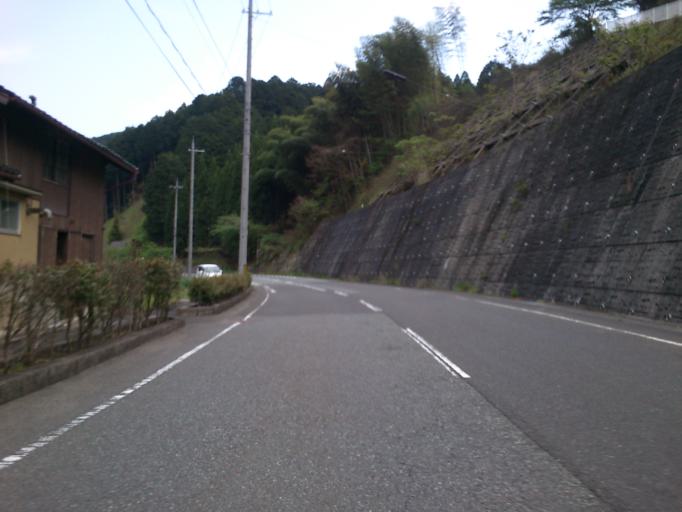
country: JP
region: Kyoto
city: Fukuchiyama
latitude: 35.3103
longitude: 135.0075
